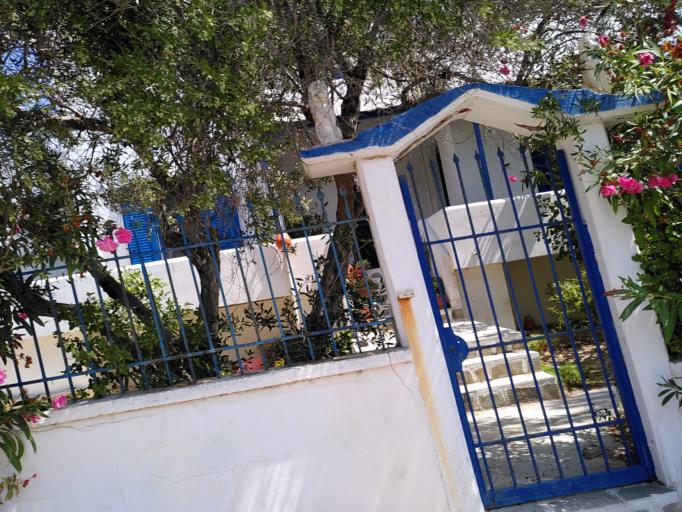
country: GR
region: South Aegean
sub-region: Nomos Kykladon
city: Amorgos
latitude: 36.9077
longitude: 25.9783
